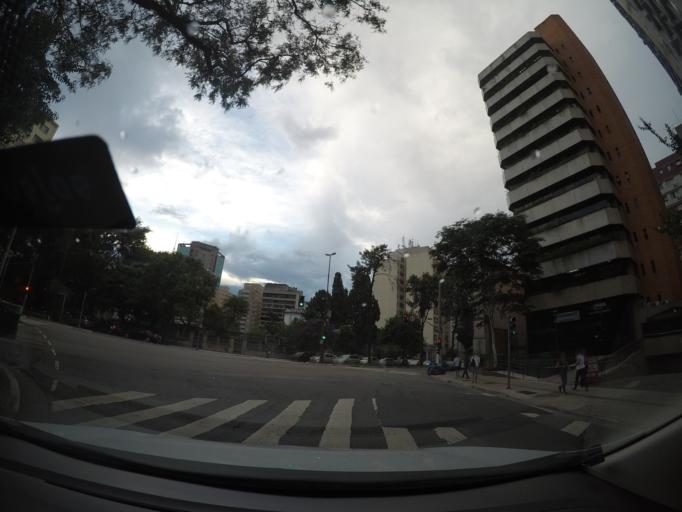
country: BR
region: Sao Paulo
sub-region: Sao Paulo
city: Sao Paulo
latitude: -23.5682
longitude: -46.6438
